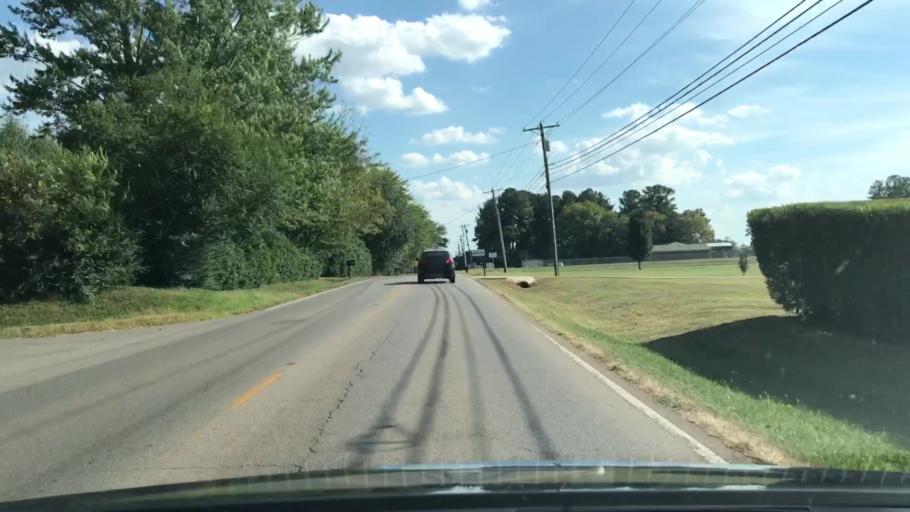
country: US
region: Alabama
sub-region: Madison County
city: Harvest
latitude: 34.8123
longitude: -86.7492
